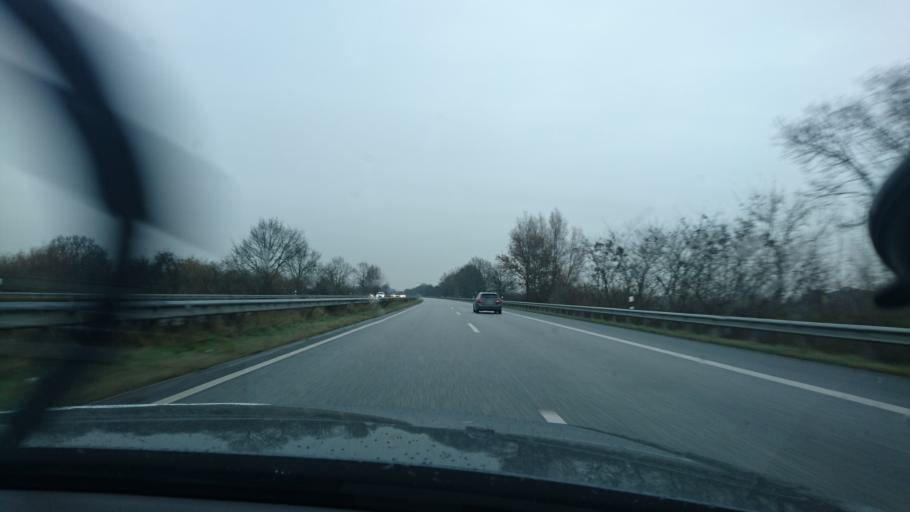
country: DE
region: Schleswig-Holstein
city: Beschendorf
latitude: 54.1715
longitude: 10.8824
